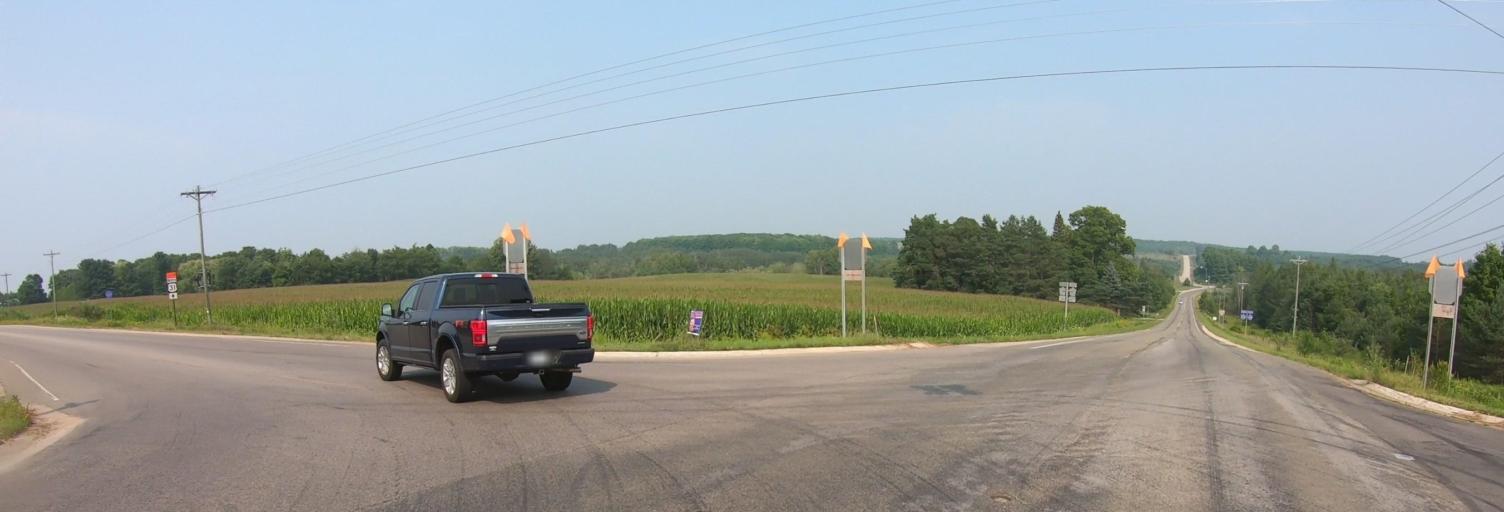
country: US
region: Michigan
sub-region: Charlevoix County
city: Charlevoix
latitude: 45.1840
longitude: -85.2637
